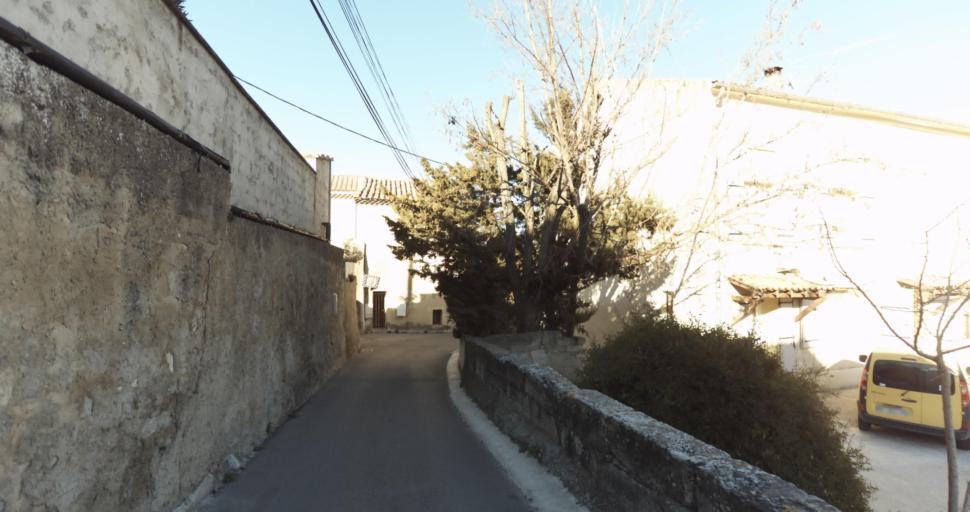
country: FR
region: Provence-Alpes-Cote d'Azur
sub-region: Departement des Bouches-du-Rhone
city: Barbentane
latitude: 43.8984
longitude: 4.7419
